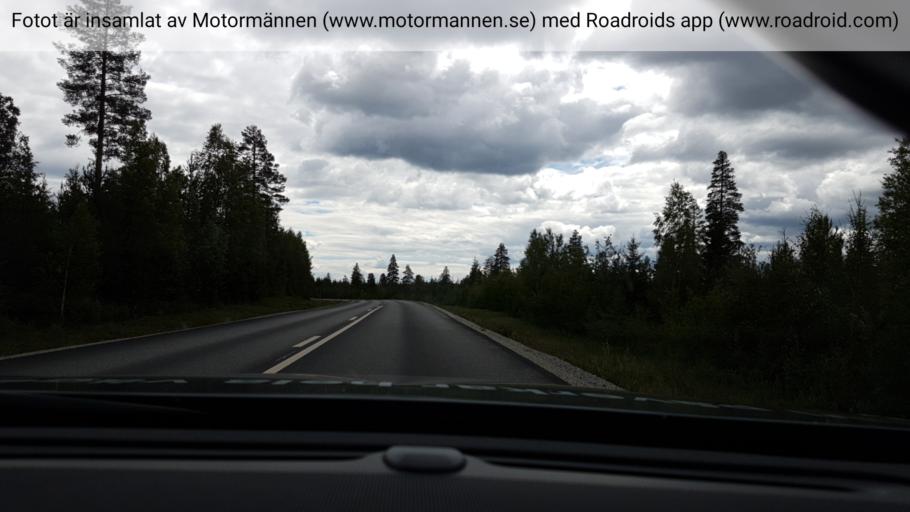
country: SE
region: Vaesterbotten
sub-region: Vindelns Kommun
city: Vindeln
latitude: 64.0739
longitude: 19.6340
